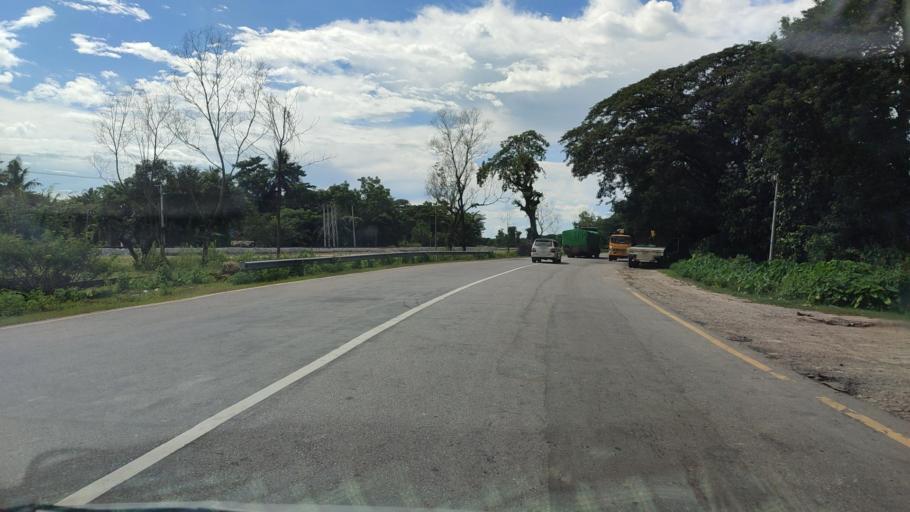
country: MM
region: Bago
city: Nyaunglebin
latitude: 18.1609
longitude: 96.6080
